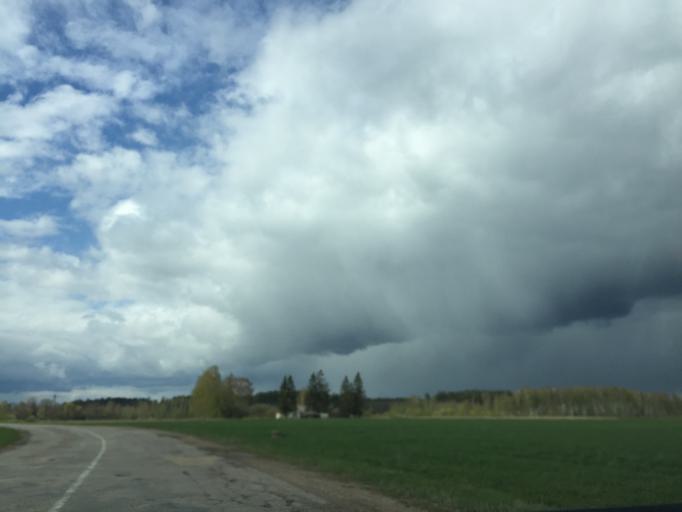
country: LV
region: Ozolnieku
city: Ozolnieki
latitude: 56.5822
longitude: 23.8234
